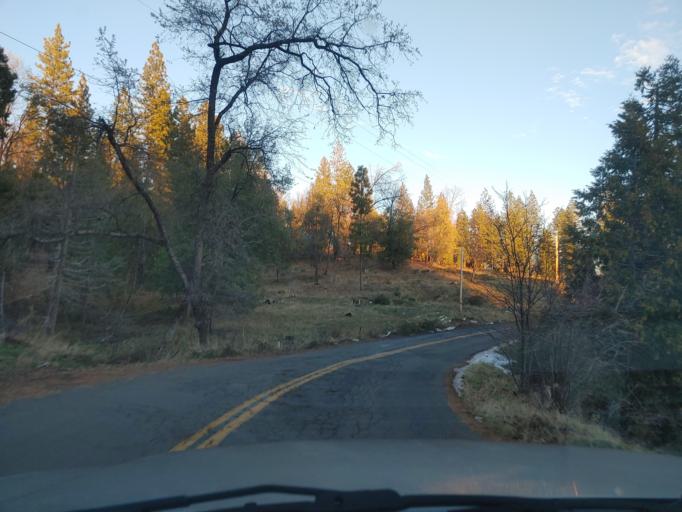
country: US
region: California
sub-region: Tuolumne County
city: Cedar Ridge
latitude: 38.0420
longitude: -120.3022
